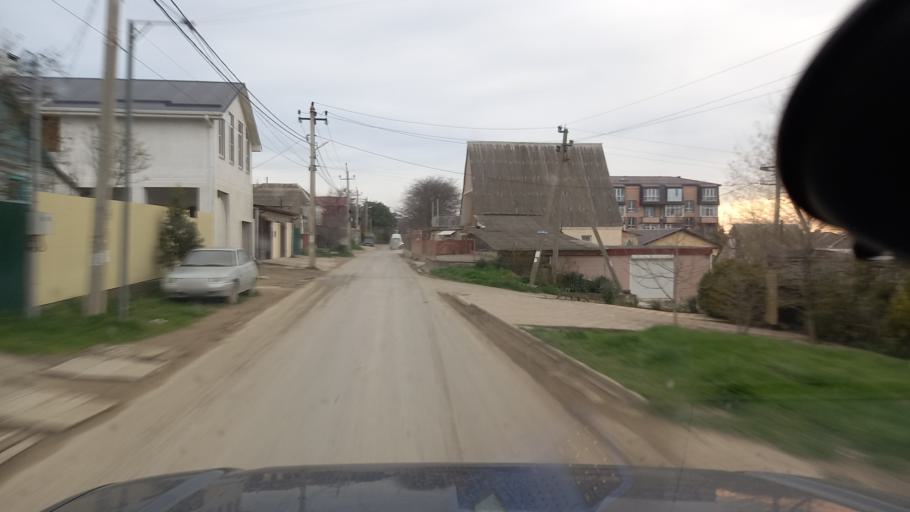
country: RU
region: Krasnodarskiy
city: Anapskaya
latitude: 44.8501
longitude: 37.3612
